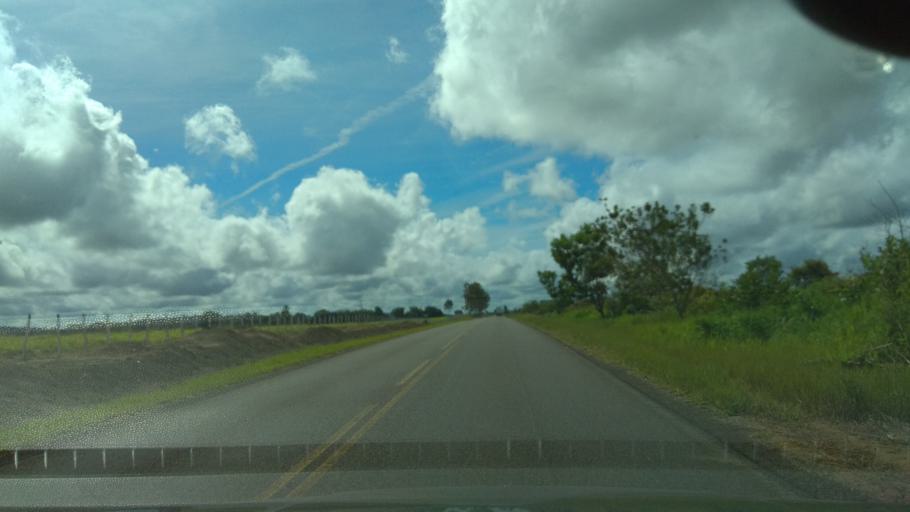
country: BR
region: Bahia
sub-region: Mutuipe
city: Mutuipe
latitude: -13.1715
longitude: -39.3532
